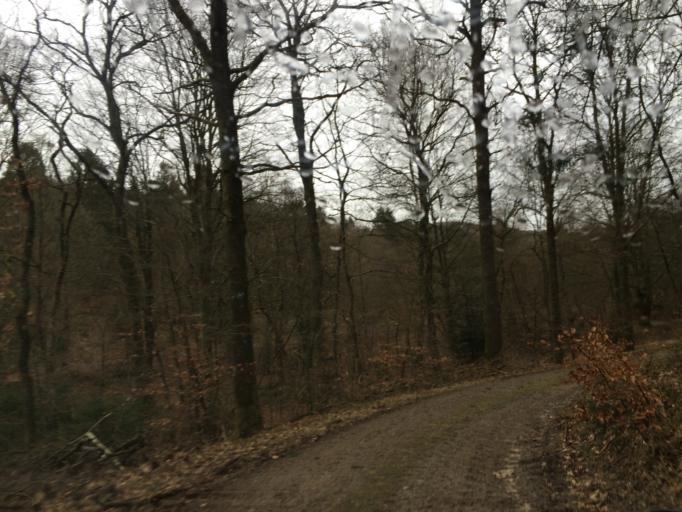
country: DK
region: Central Jutland
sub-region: Silkeborg Kommune
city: Virklund
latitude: 56.0363
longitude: 9.4835
